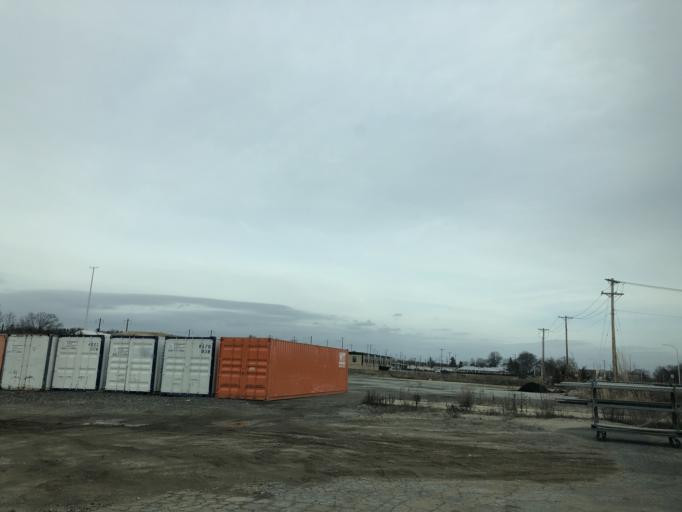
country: US
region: Delaware
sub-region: New Castle County
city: Newark
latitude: 39.6659
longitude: -75.7589
